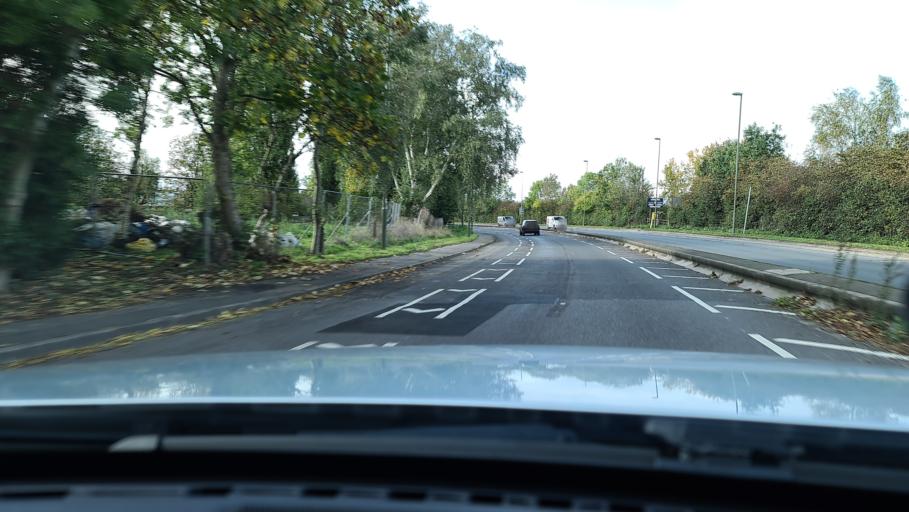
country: GB
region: England
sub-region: Surrey
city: Esher
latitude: 51.3688
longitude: -0.3792
